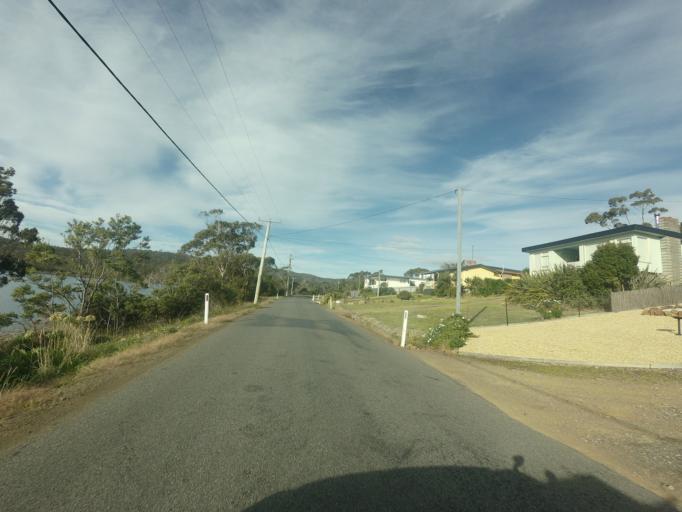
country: AU
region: Tasmania
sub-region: Sorell
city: Sorell
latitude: -42.9460
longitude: 147.8584
